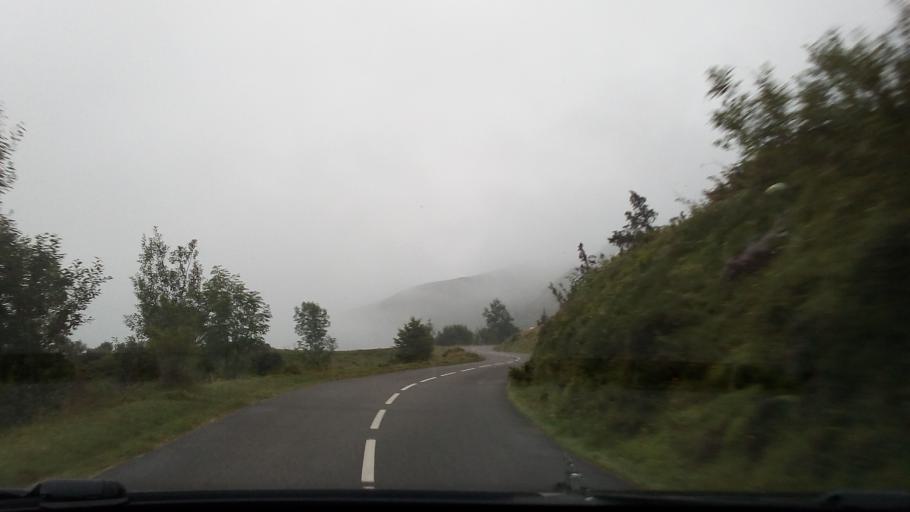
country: FR
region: Aquitaine
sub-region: Departement des Pyrenees-Atlantiques
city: Laruns
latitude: 42.9543
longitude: -0.2857
